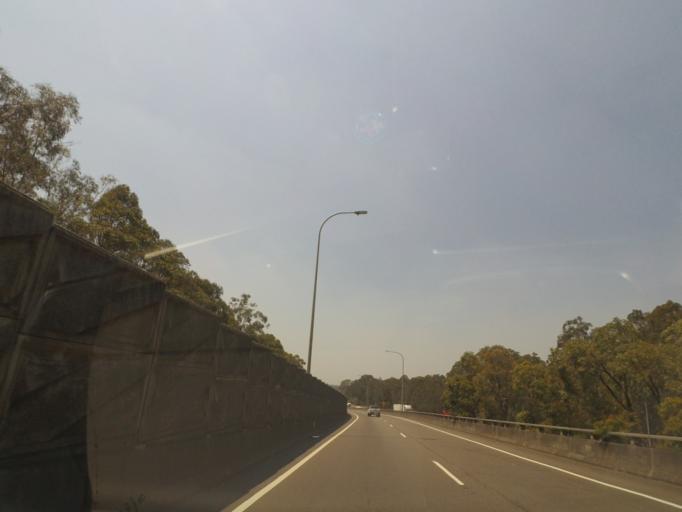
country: AU
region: New South Wales
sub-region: Newcastle
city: Beresfield
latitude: -32.8106
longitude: 151.6493
